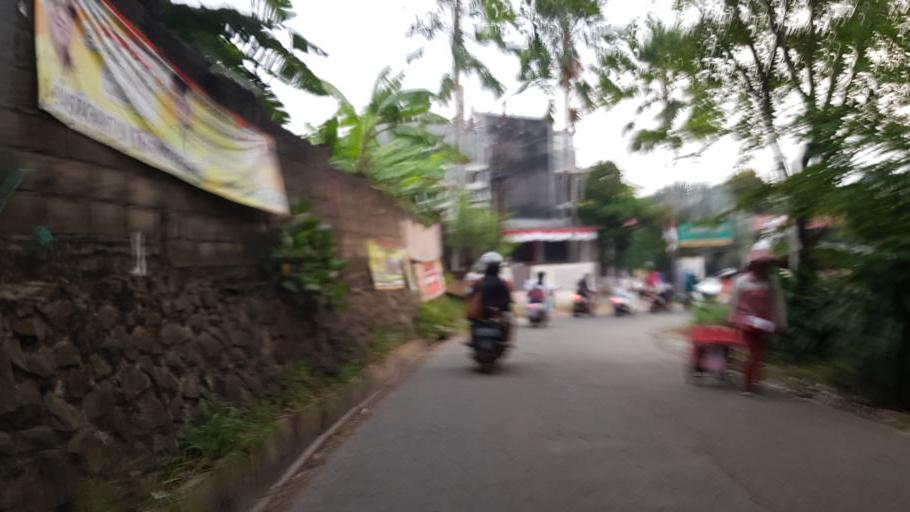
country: ID
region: West Java
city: Depok
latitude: -6.3713
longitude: 106.7971
